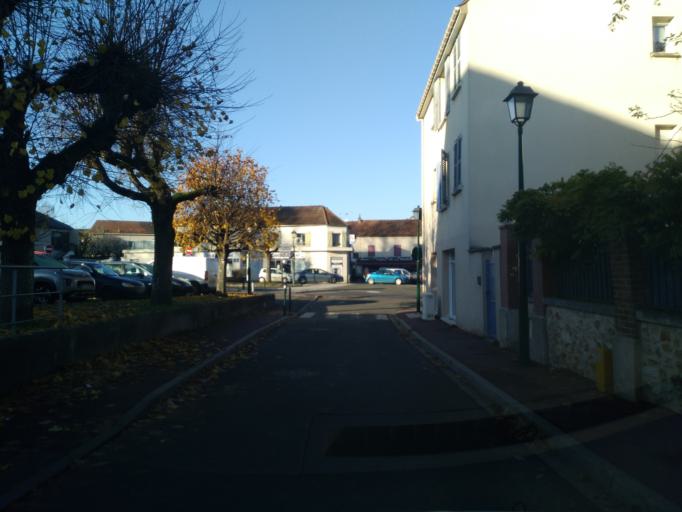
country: FR
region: Ile-de-France
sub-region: Departement des Yvelines
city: Plaisir
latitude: 48.8167
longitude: 1.9489
